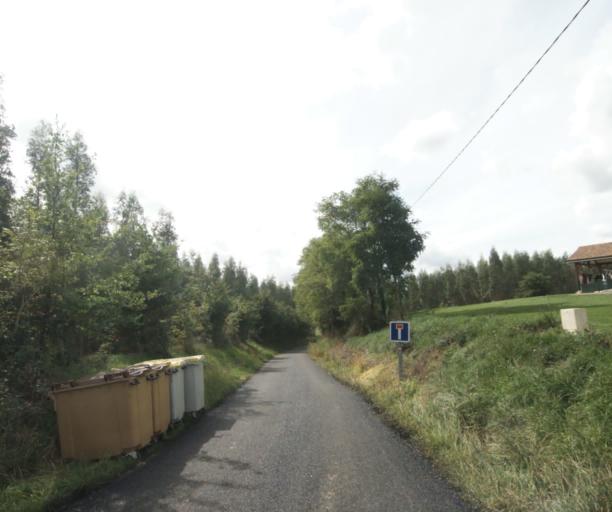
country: FR
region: Midi-Pyrenees
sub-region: Departement du Gers
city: Eauze
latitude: 43.8479
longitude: 0.0781
